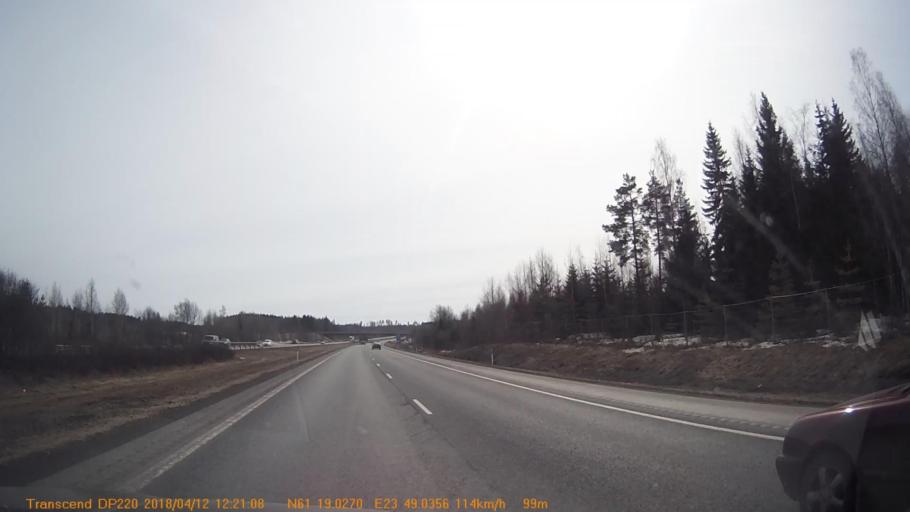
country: FI
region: Pirkanmaa
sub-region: Tampere
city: Lempaeaelae
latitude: 61.3165
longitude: 23.8179
